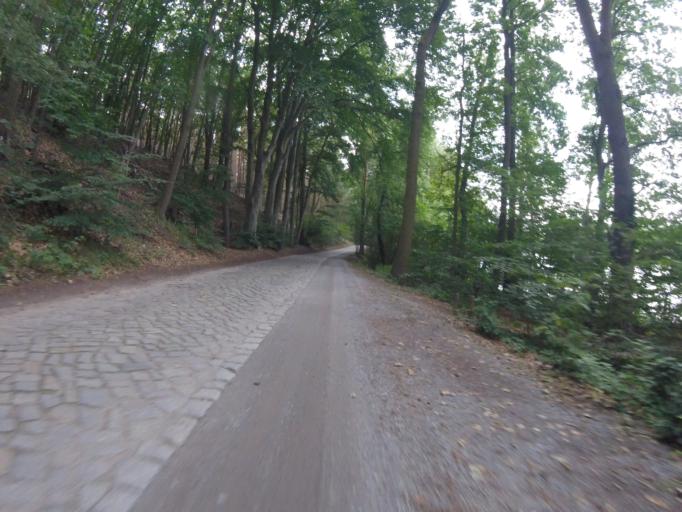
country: DE
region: Brandenburg
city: Schwerin
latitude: 52.1901
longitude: 13.5926
